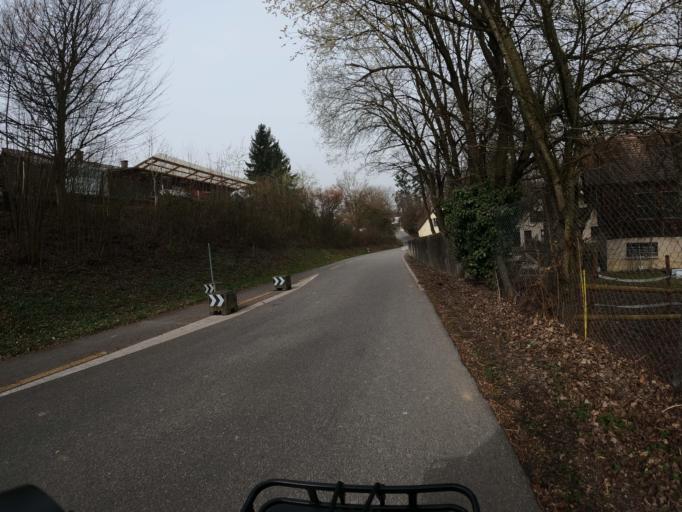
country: CH
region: Aargau
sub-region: Bezirk Baden
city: Mellingen
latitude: 47.4100
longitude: 8.2623
